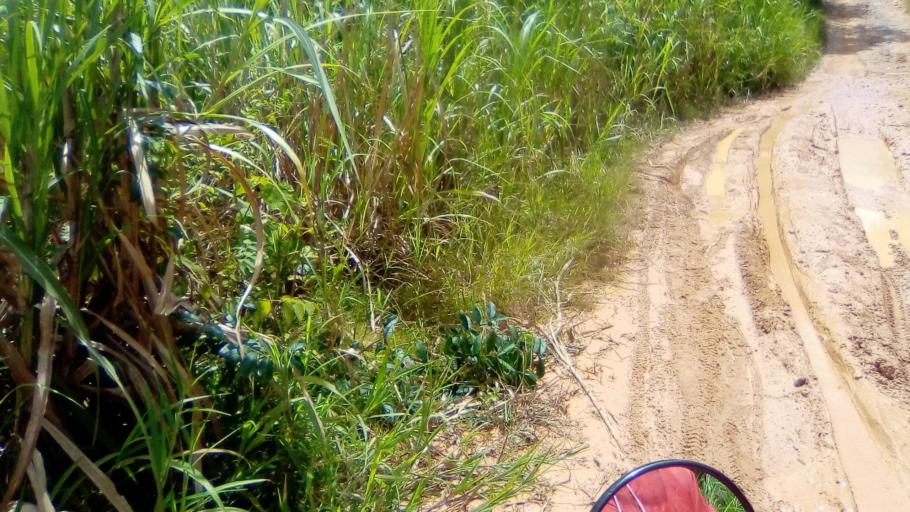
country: SL
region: Eastern Province
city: Simbakoro
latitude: 8.5408
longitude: -10.9398
